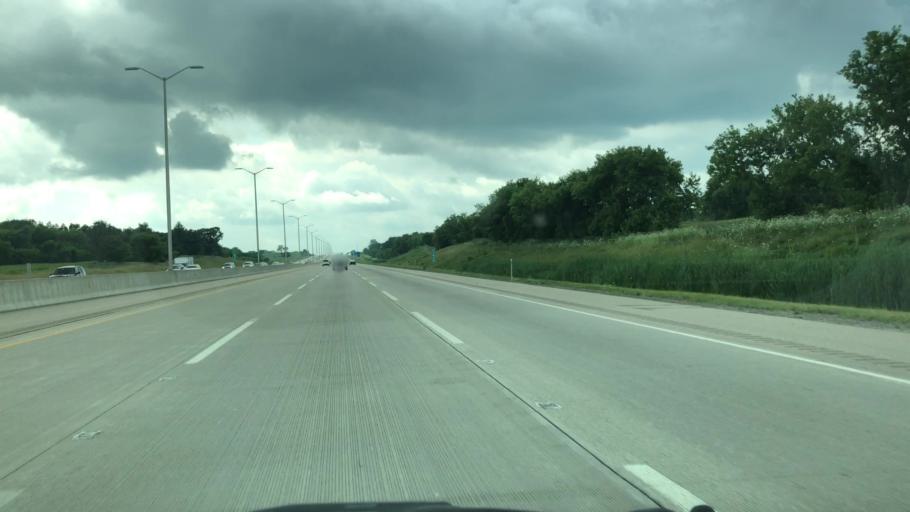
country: US
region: Illinois
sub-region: Kane County
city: Hampshire
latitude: 42.1371
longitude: -88.4841
